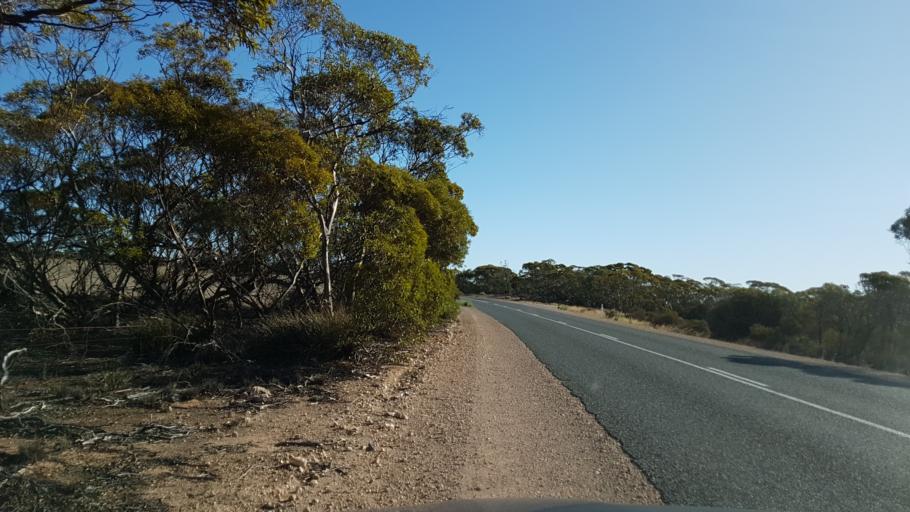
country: AU
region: South Australia
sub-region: Mid Murray
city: Mannum
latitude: -34.7956
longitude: 139.5040
